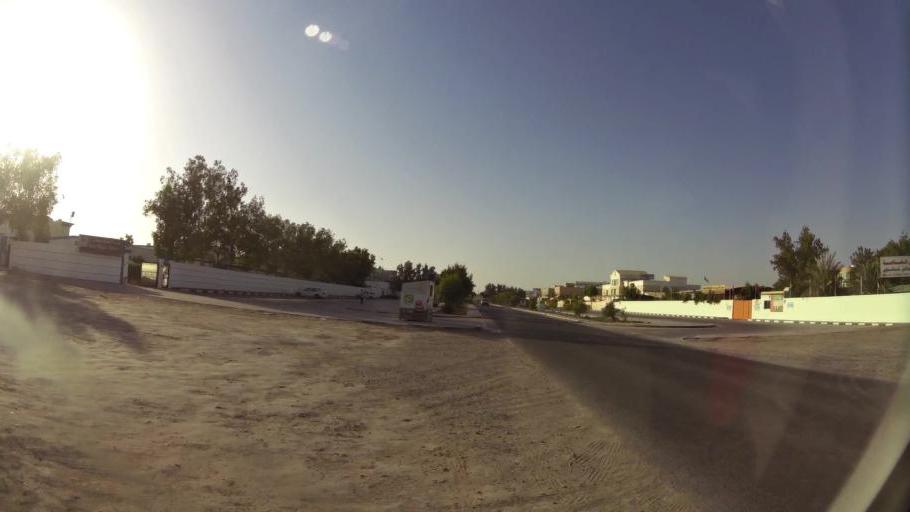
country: AE
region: Ajman
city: Ajman
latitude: 25.3979
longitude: 55.4936
